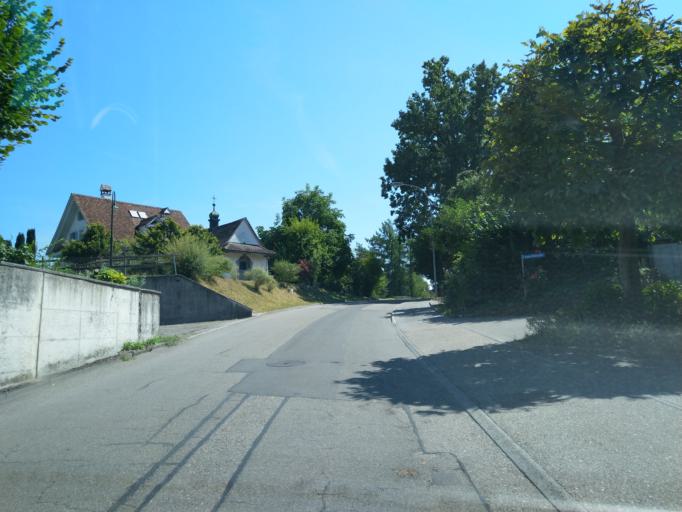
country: CH
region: Lucerne
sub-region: Hochdorf District
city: Ballwil
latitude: 47.1312
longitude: 8.3193
